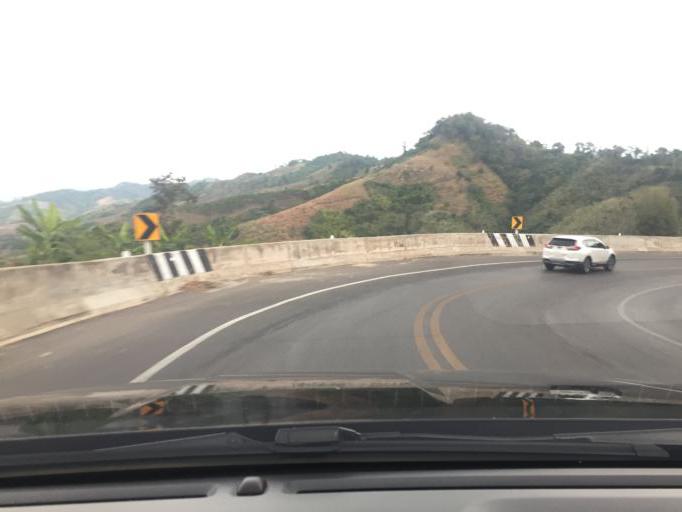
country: TH
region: Nan
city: Ban Luang
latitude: 18.8713
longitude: 100.5505
